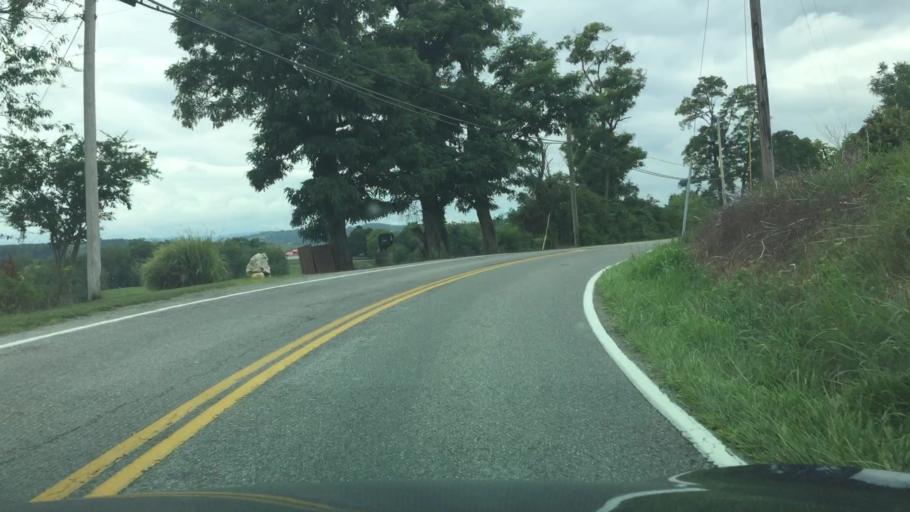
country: US
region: Virginia
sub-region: Pulaski County
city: Pulaski
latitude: 37.0079
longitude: -80.7435
